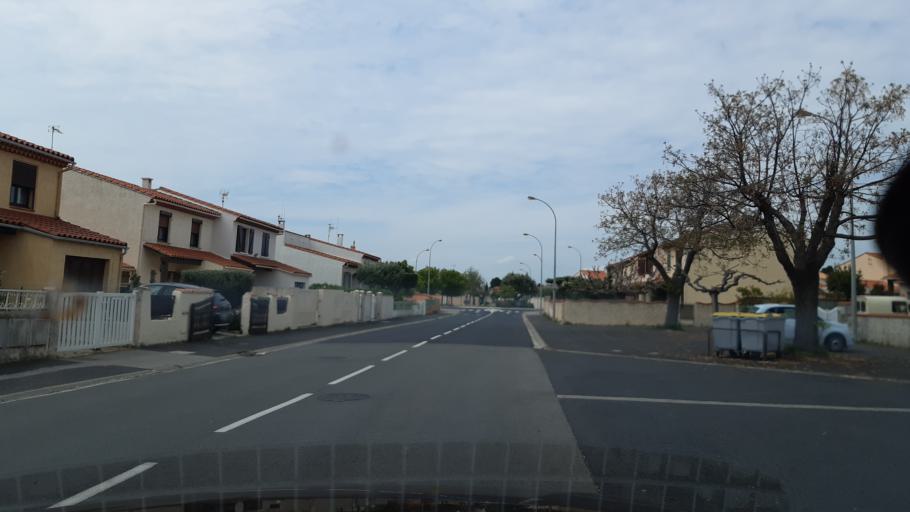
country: FR
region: Languedoc-Roussillon
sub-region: Departement de l'Aude
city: Narbonne
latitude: 43.1875
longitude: 3.0283
